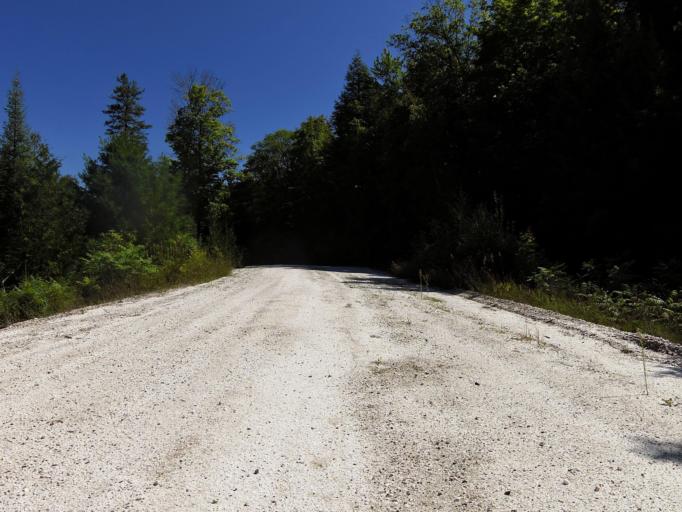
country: CA
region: Ontario
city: Arnprior
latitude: 45.1586
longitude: -76.4938
